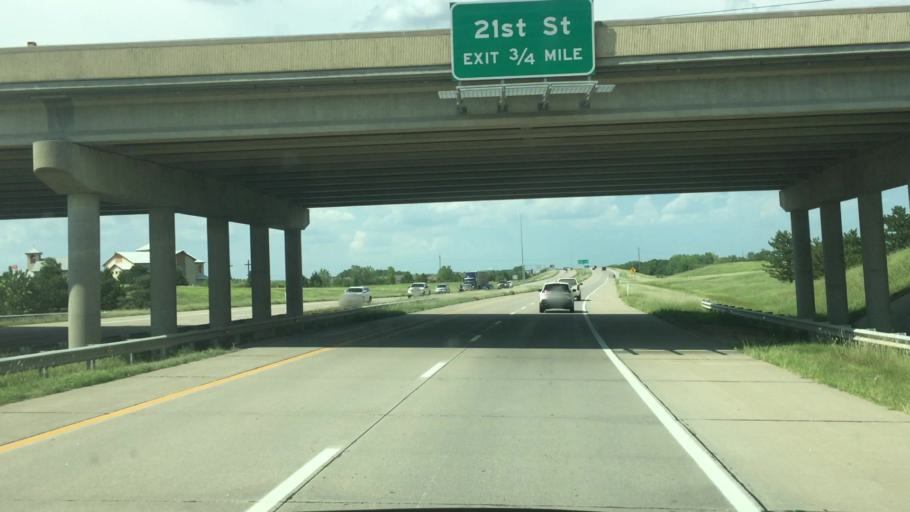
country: US
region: Kansas
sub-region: Butler County
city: Andover
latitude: 37.7083
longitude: -97.2003
